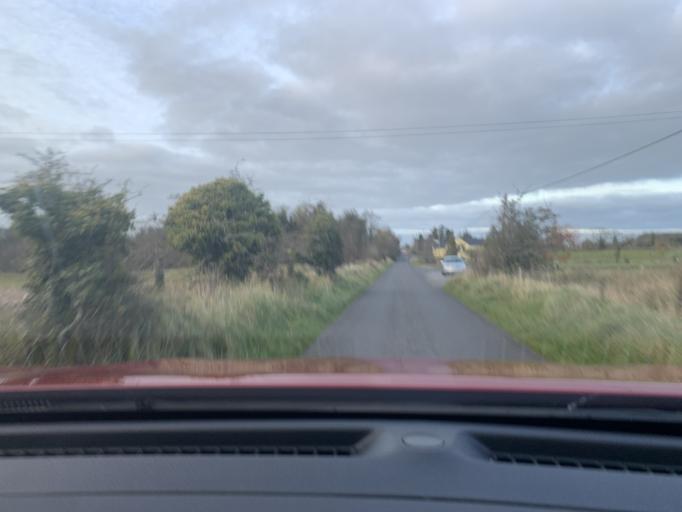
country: IE
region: Connaught
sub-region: Roscommon
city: Ballaghaderreen
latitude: 53.9735
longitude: -8.6222
